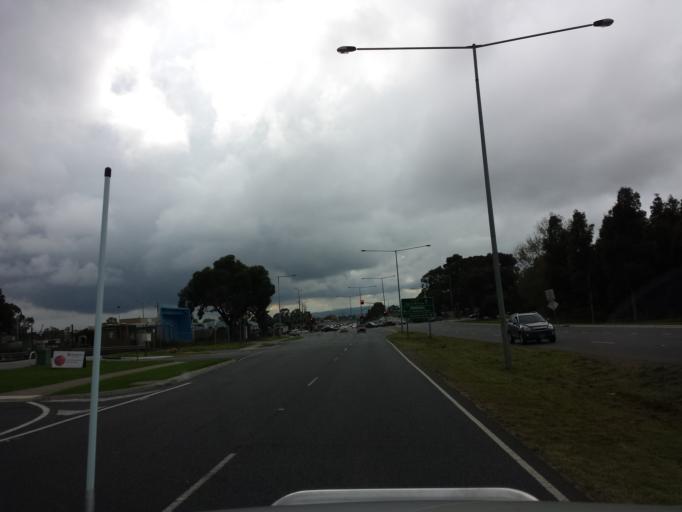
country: AU
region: Victoria
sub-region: Casey
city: Narre Warren
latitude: -38.0328
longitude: 145.3057
